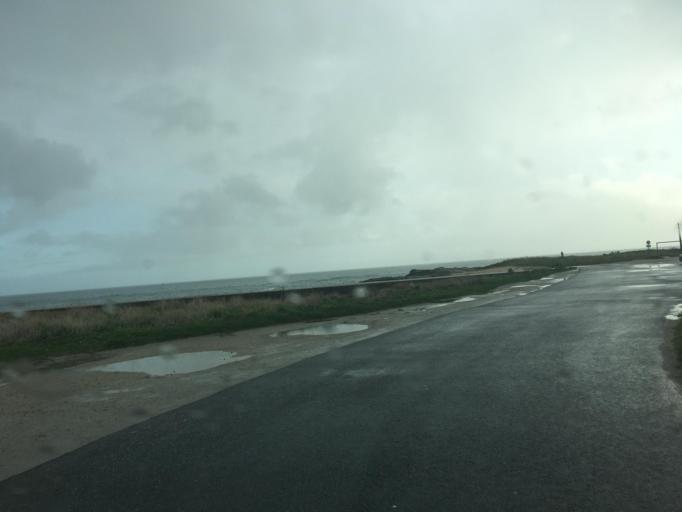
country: FR
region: Lower Normandy
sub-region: Departement de la Manche
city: Reville
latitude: 49.6949
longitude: -1.2678
